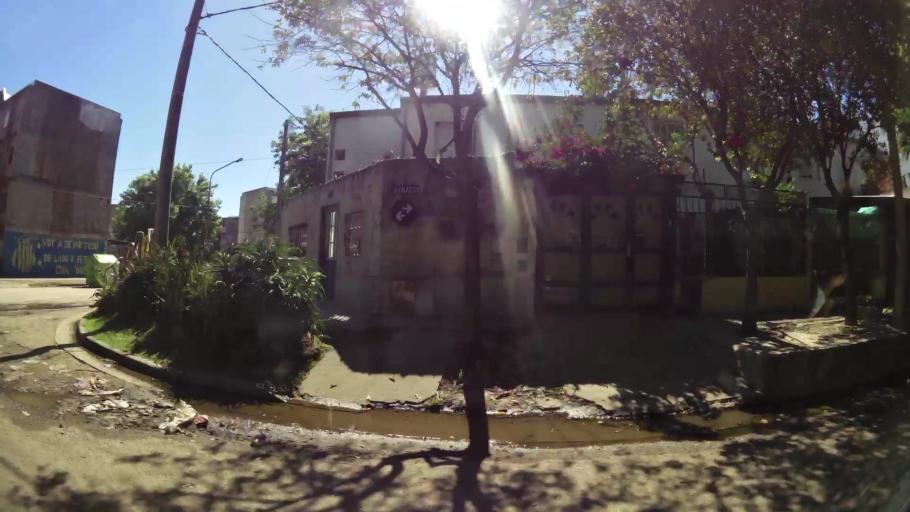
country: AR
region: Santa Fe
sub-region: Departamento de Rosario
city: Rosario
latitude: -32.9732
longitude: -60.6993
